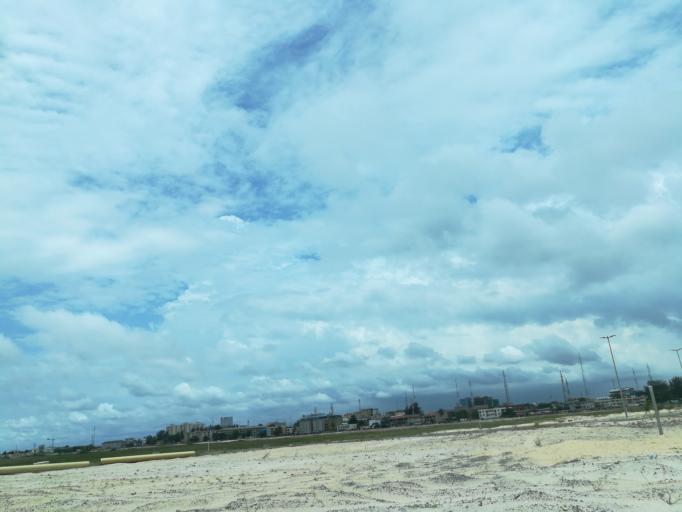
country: NG
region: Lagos
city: Ikoyi
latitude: 6.4186
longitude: 3.4244
